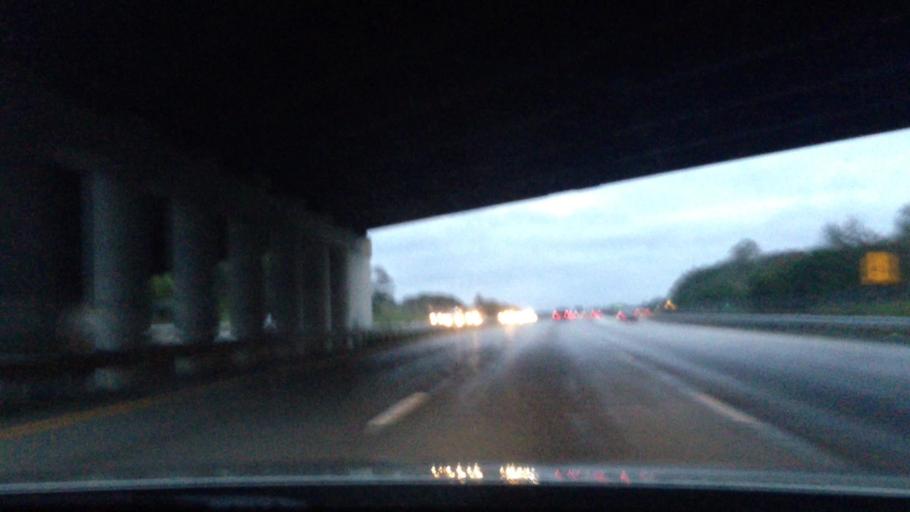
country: US
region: New York
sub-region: Suffolk County
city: Oakdale
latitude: 40.7520
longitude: -73.1251
